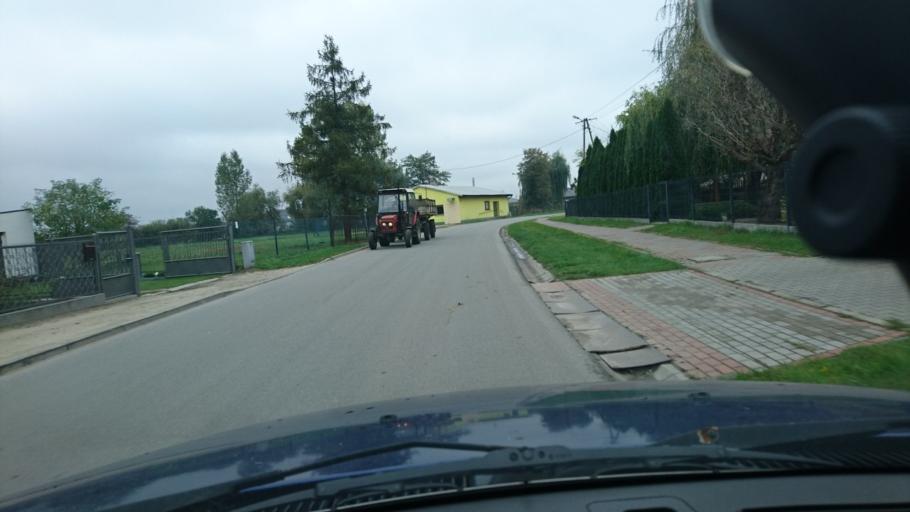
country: PL
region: Greater Poland Voivodeship
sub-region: Powiat krotoszynski
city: Sulmierzyce
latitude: 51.5682
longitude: 17.5850
